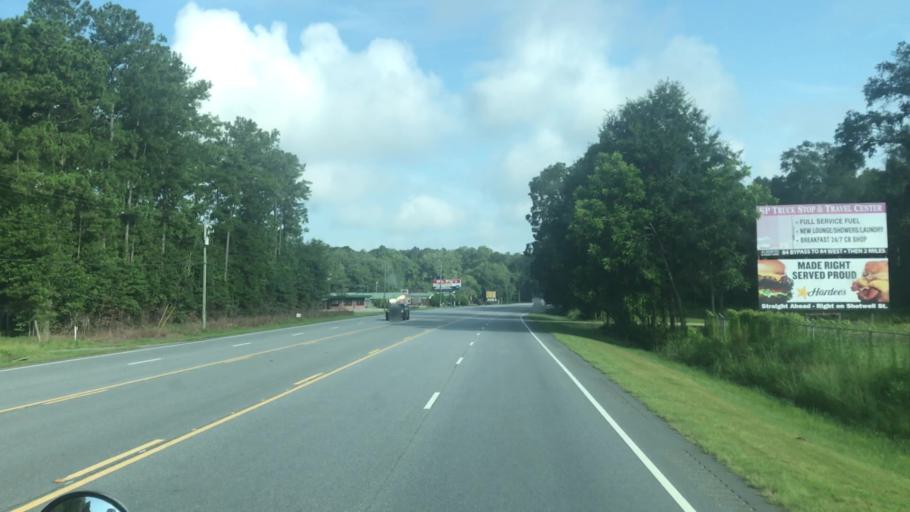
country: US
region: Georgia
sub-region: Decatur County
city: Bainbridge
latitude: 30.8691
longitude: -84.5591
